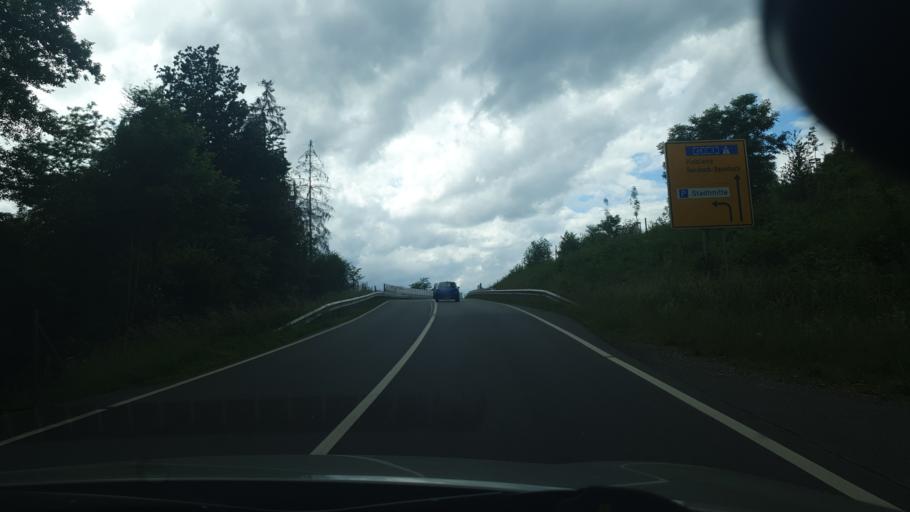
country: DE
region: Rheinland-Pfalz
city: Hohr-Grenzhausen
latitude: 50.4220
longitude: 7.6841
